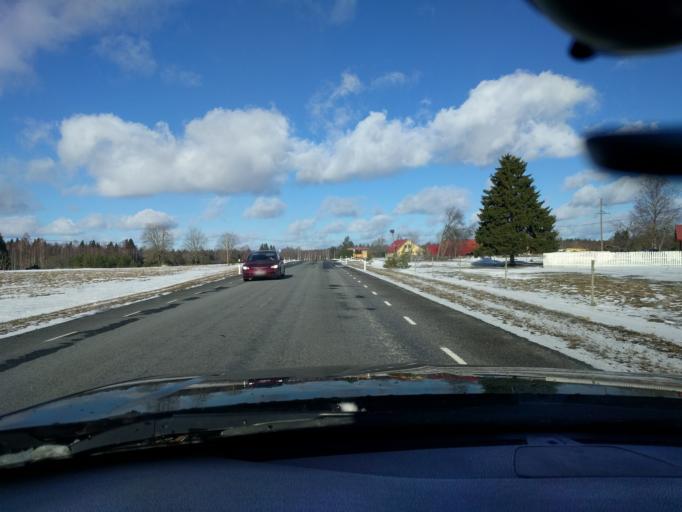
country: EE
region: Harju
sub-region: Anija vald
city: Kehra
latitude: 59.2306
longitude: 25.3893
